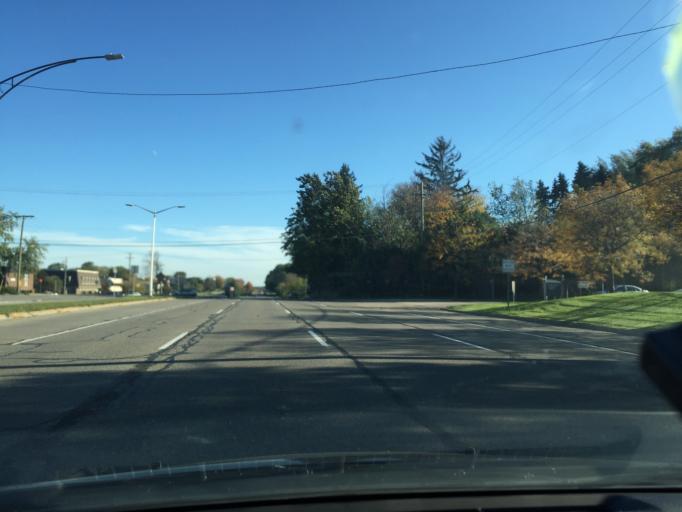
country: US
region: Michigan
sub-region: Oakland County
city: Pontiac
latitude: 42.6132
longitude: -83.2735
